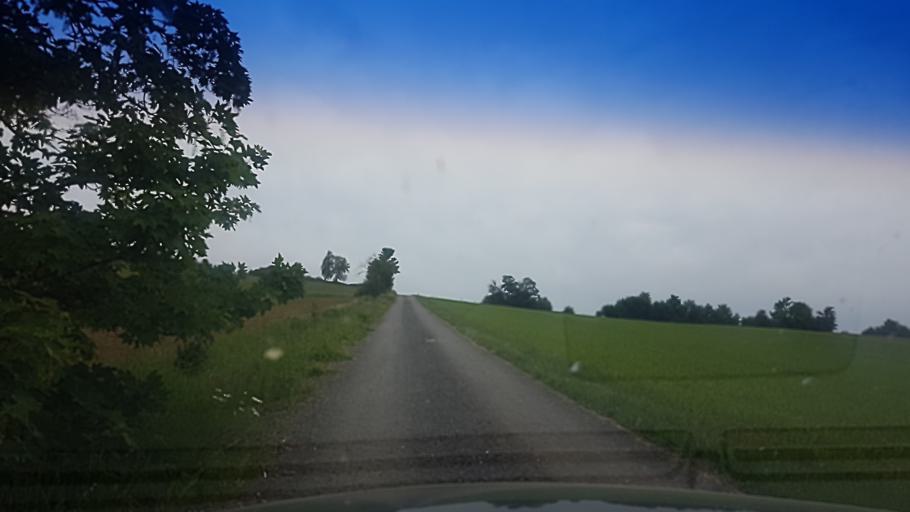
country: DE
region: Bavaria
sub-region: Upper Franconia
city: Buttenheim
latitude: 49.8124
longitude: 11.0410
